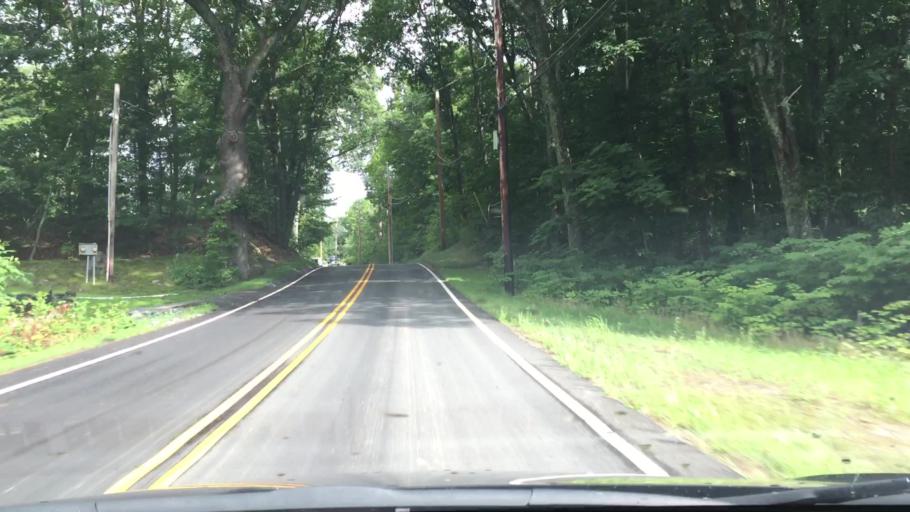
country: US
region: Massachusetts
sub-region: Middlesex County
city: Littleton Common
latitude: 42.5223
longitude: -71.4588
